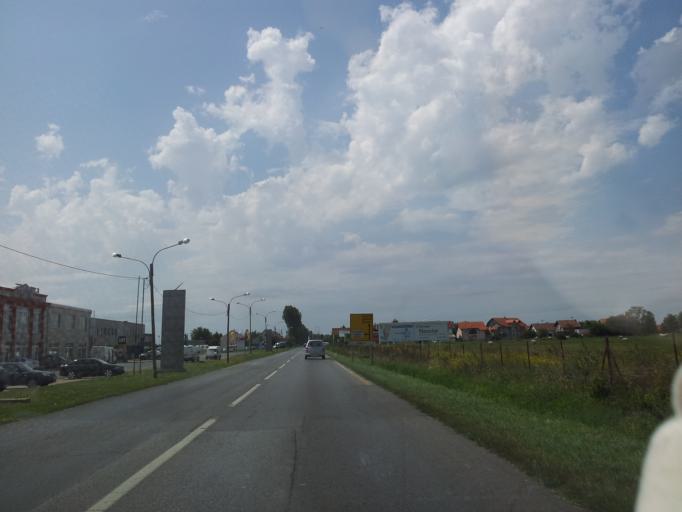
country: HR
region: Osjecko-Baranjska
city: Brijest
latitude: 45.5389
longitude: 18.6425
